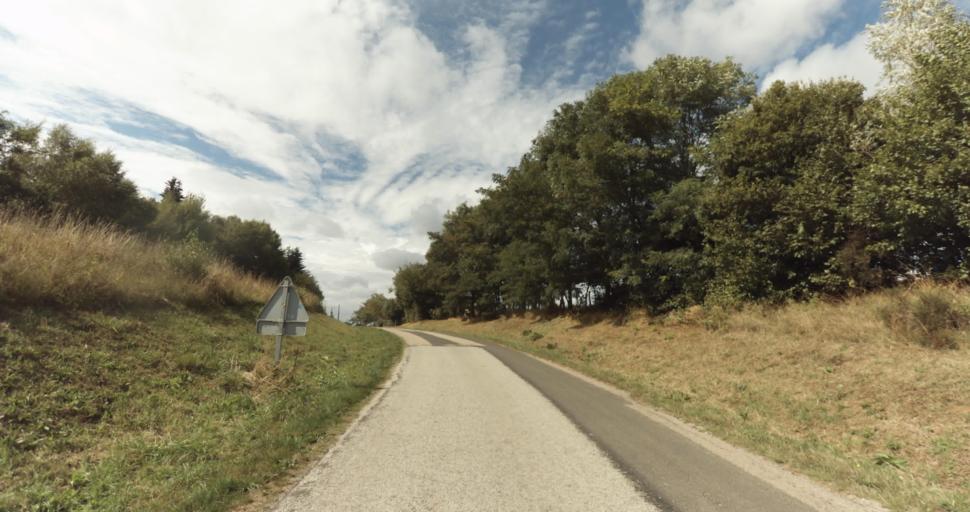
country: FR
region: Lower Normandy
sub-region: Departement de l'Orne
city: Gace
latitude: 48.7853
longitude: 0.3171
